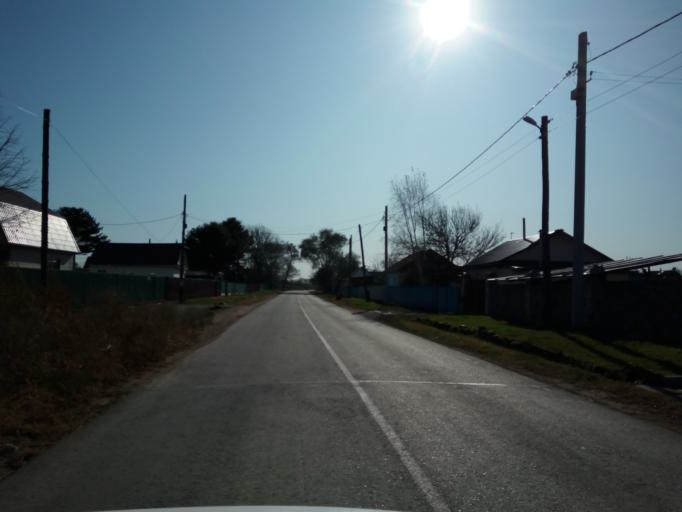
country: RU
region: Primorskiy
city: Dal'nerechensk
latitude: 45.9359
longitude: 133.7057
